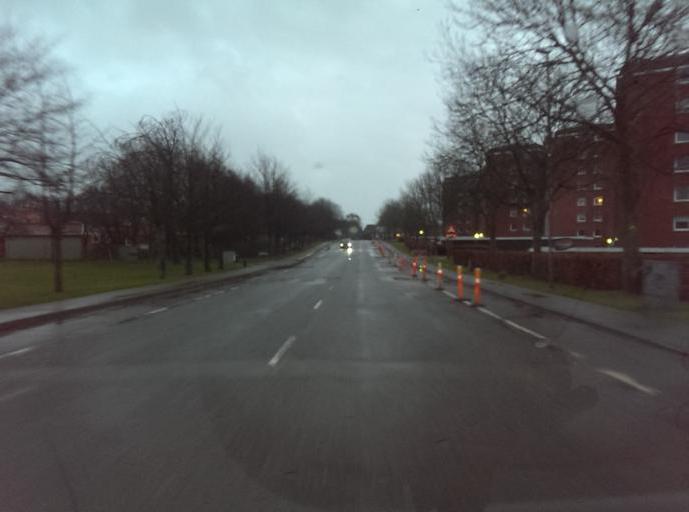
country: DK
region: South Denmark
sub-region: Esbjerg Kommune
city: Esbjerg
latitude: 55.4839
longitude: 8.4528
